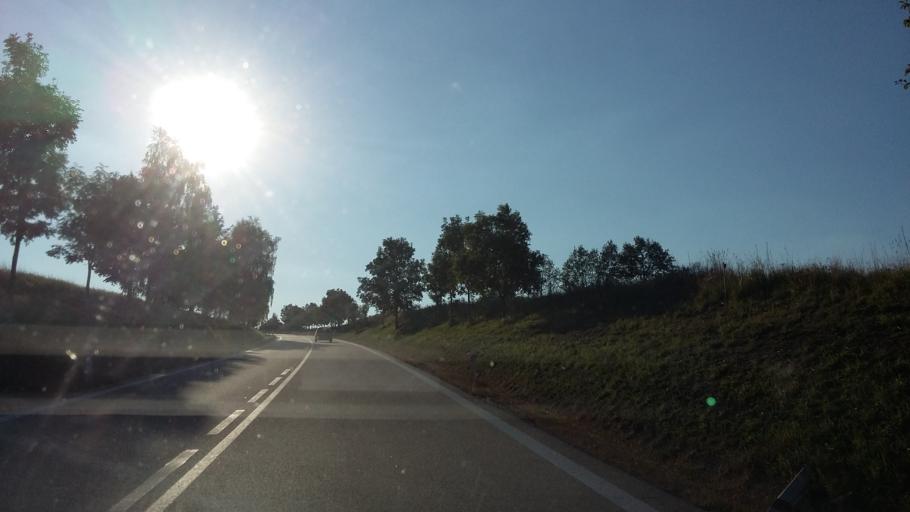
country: CZ
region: Vysocina
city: Merin
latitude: 49.4003
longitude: 15.8522
